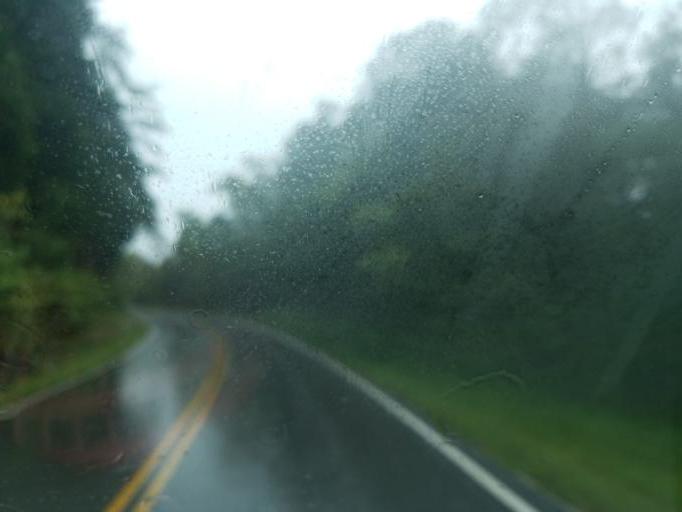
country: US
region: Kentucky
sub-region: Carter County
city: Grayson
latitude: 38.4910
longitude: -82.9891
